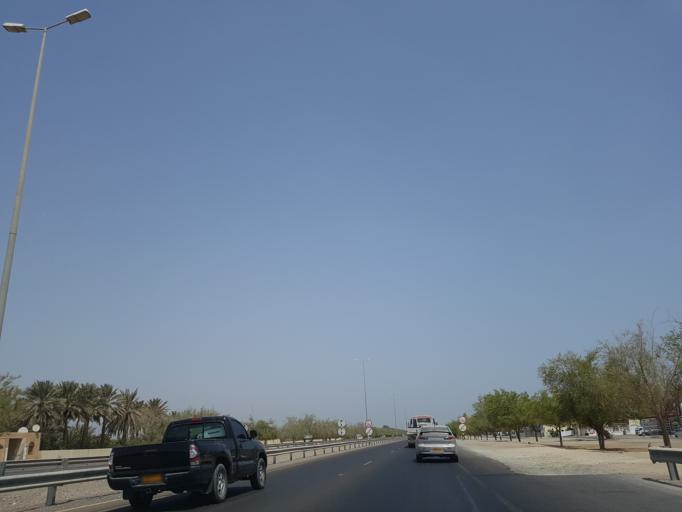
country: OM
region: Al Batinah
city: Saham
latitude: 24.1570
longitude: 56.8650
